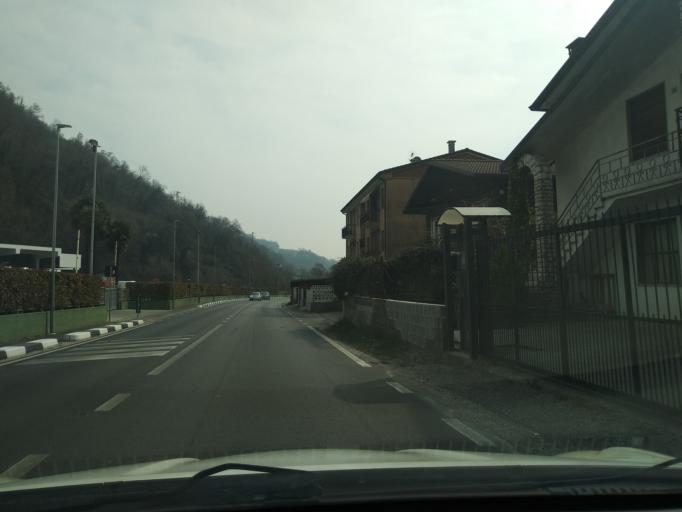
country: IT
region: Veneto
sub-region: Provincia di Vicenza
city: Nogarole Vicentino
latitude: 45.5619
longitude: 11.2677
